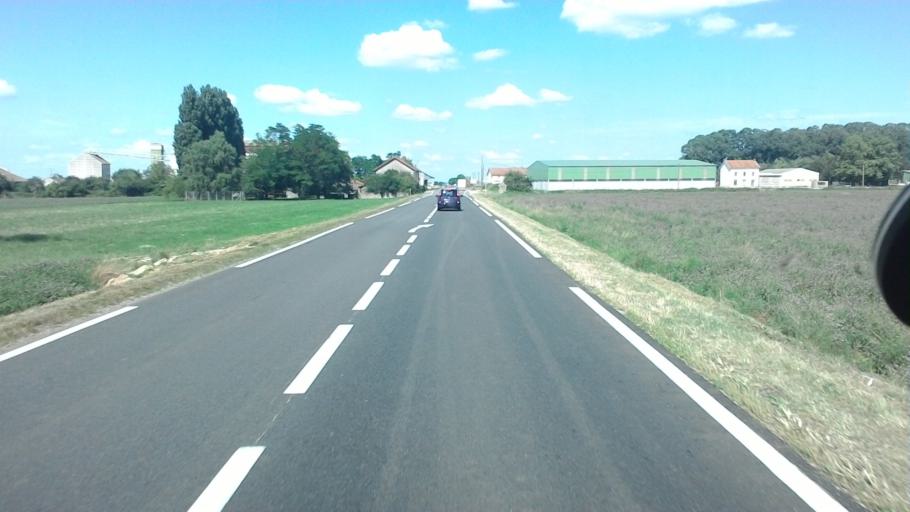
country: FR
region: Franche-Comte
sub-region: Departement du Jura
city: Saint-Aubin
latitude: 46.9939
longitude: 5.3399
